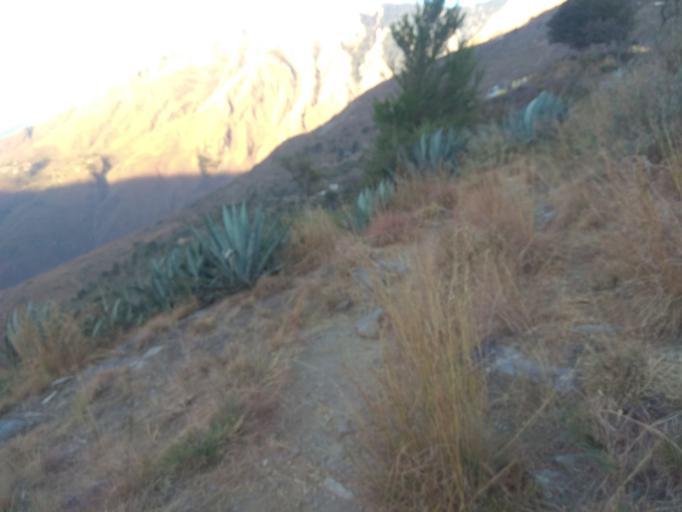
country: NP
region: Mid Western
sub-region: Bheri Zone
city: Dailekh
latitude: 29.2858
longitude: 81.7166
